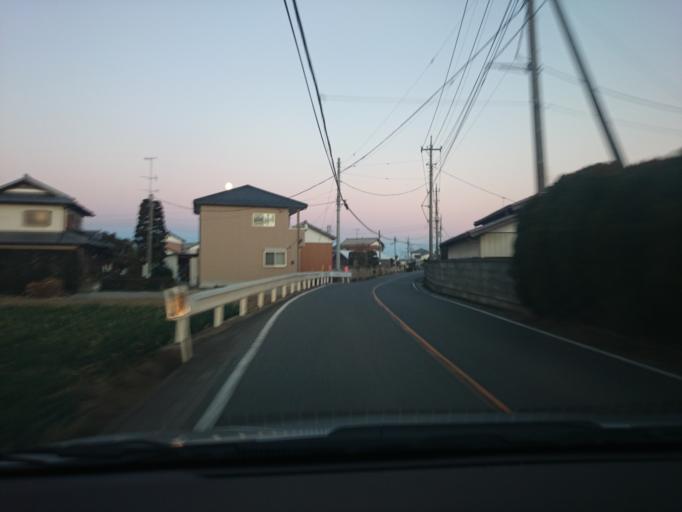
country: JP
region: Saitama
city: Fukayacho
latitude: 36.2297
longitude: 139.2822
